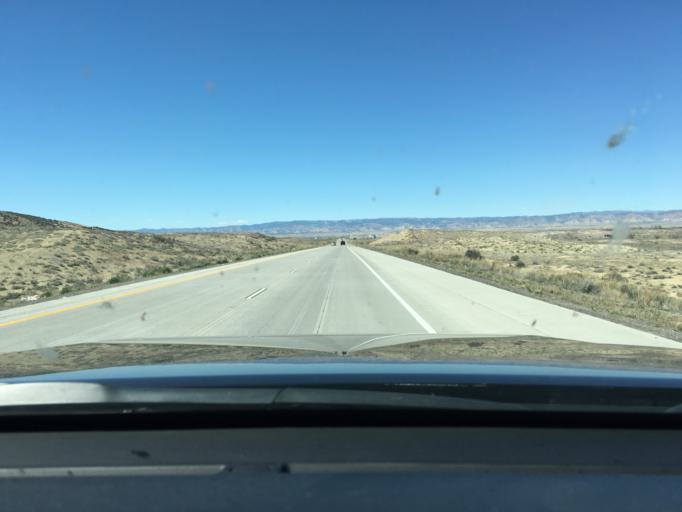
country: US
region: Colorado
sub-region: Mesa County
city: Loma
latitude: 39.2075
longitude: -108.8592
